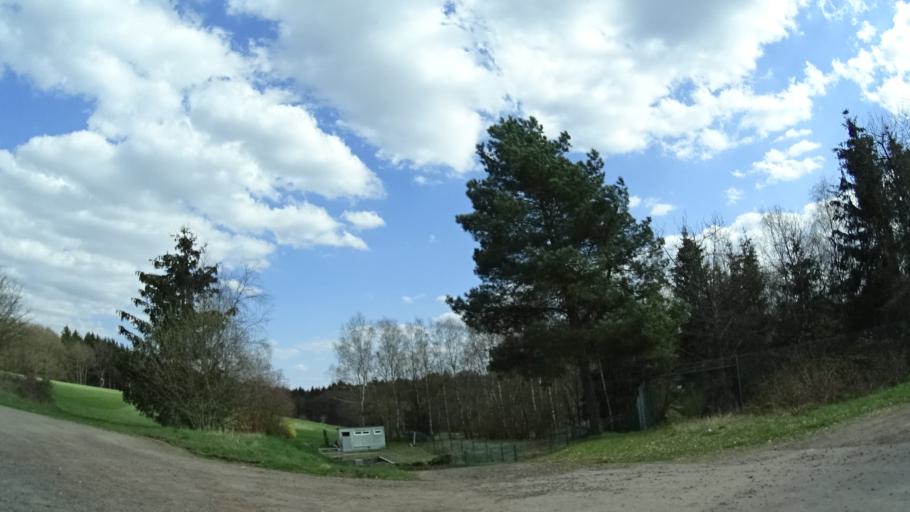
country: DE
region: Rheinland-Pfalz
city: Herborn
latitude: 49.7659
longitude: 7.2992
